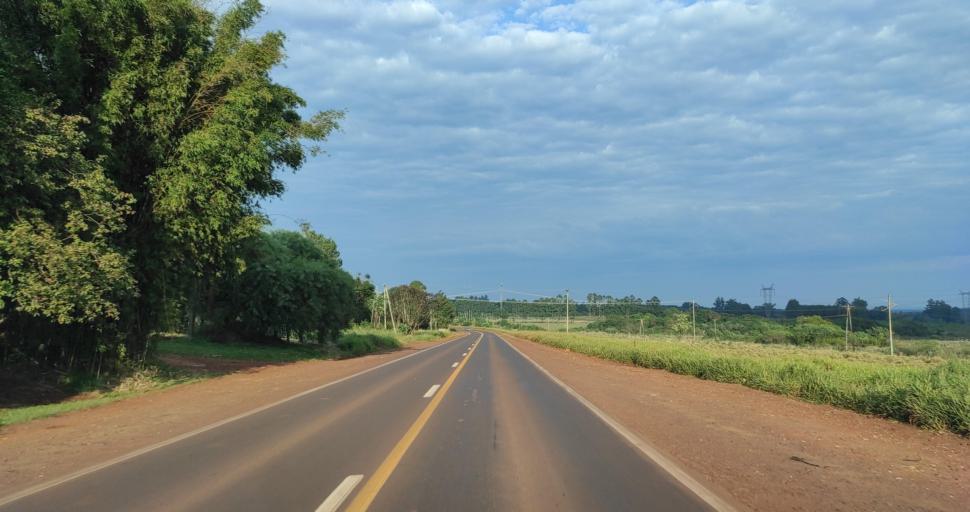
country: AR
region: Corrientes
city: Gobernador Ingeniero Valentin Virasoro
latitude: -27.9544
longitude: -55.9974
